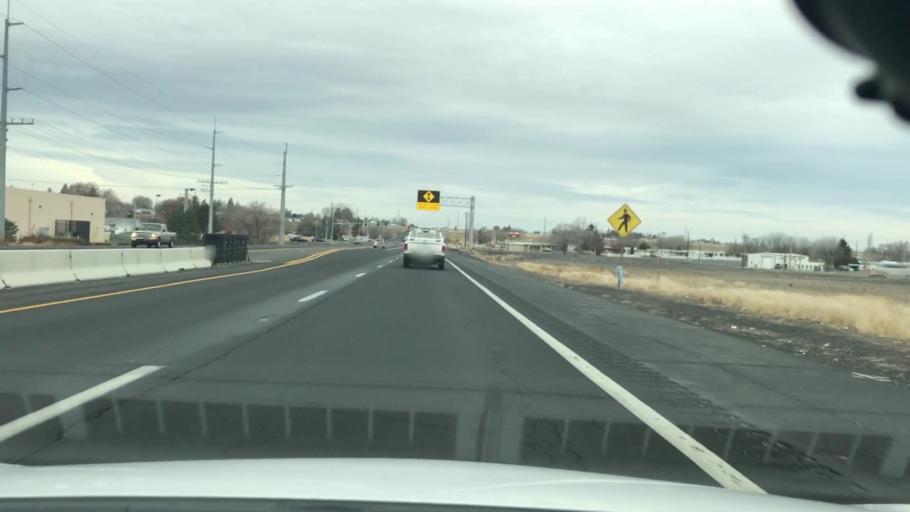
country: US
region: Washington
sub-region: Grant County
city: Moses Lake
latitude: 47.1484
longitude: -119.2909
